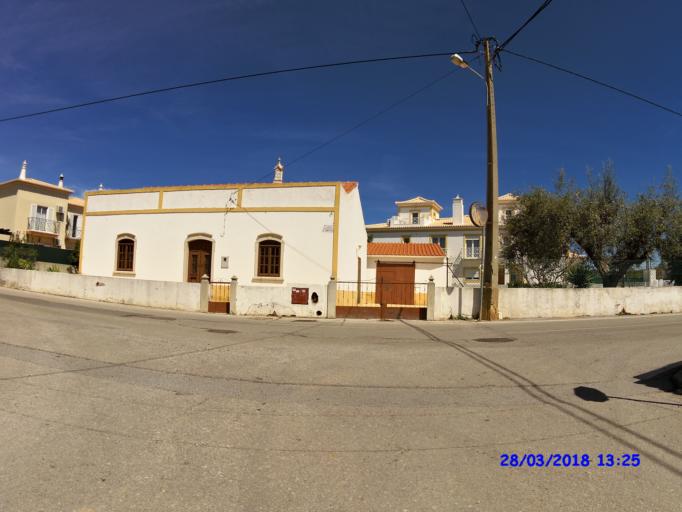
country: PT
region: Faro
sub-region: Albufeira
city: Ferreiras
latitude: 37.1296
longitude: -8.2328
